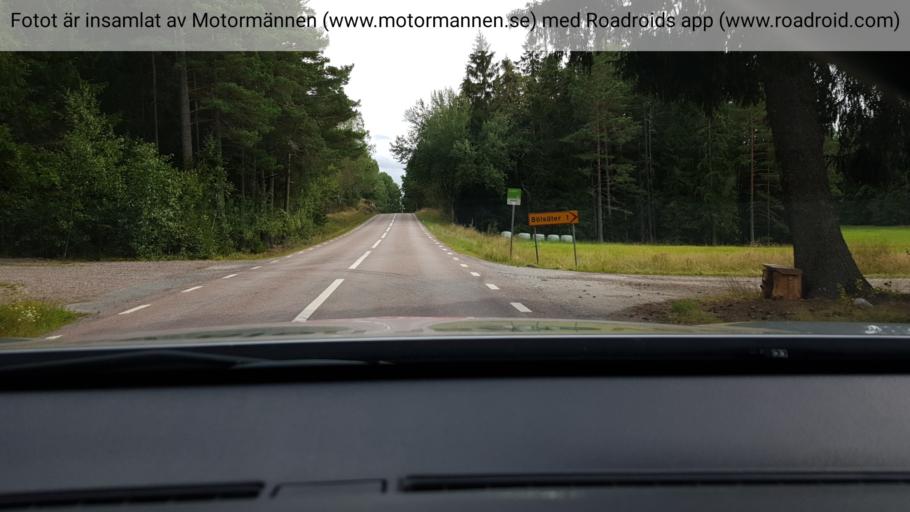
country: SE
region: Soedermanland
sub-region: Gnesta Kommun
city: Gnesta
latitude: 58.9718
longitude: 17.1467
